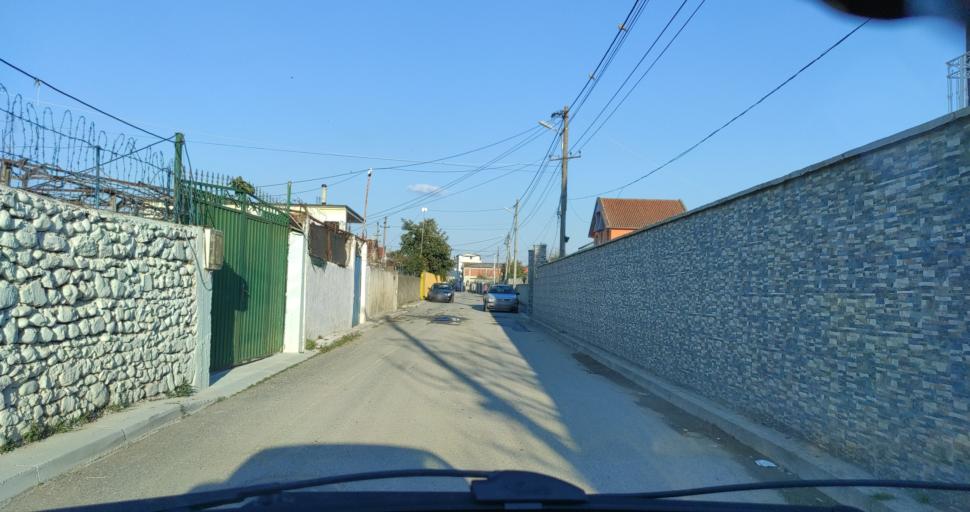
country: AL
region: Shkoder
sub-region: Rrethi i Shkodres
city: Shkoder
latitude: 42.0785
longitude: 19.4958
